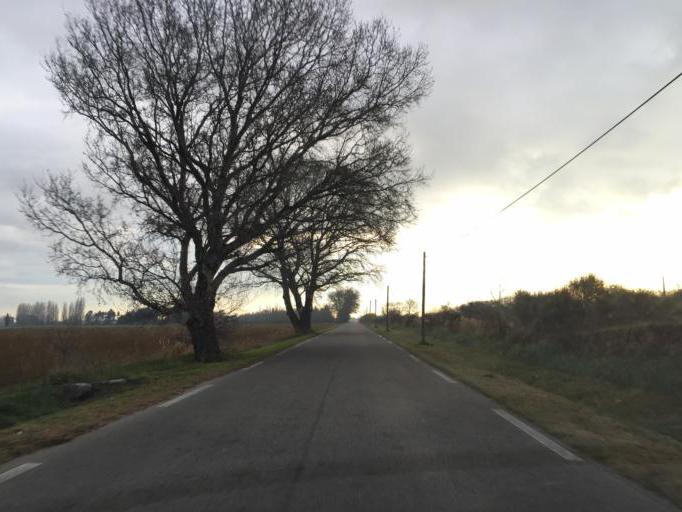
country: FR
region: Provence-Alpes-Cote d'Azur
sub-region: Departement du Vaucluse
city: Camaret-sur-Aigues
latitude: 44.1293
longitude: 4.8569
